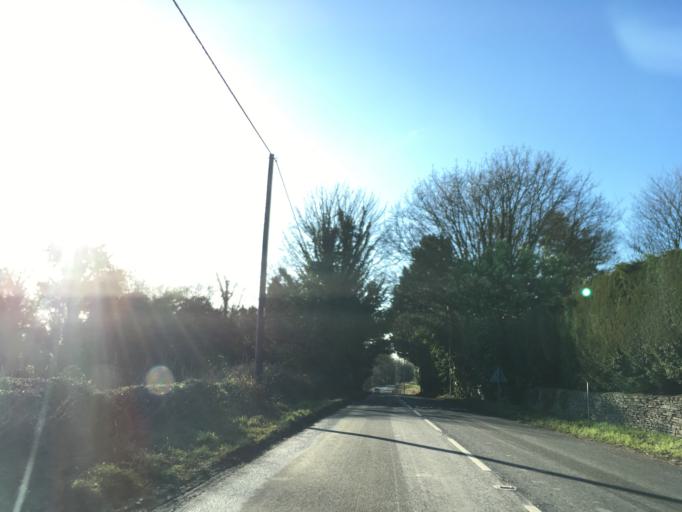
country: GB
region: England
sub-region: Wiltshire
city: Charlton
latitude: 51.5985
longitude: -2.0565
